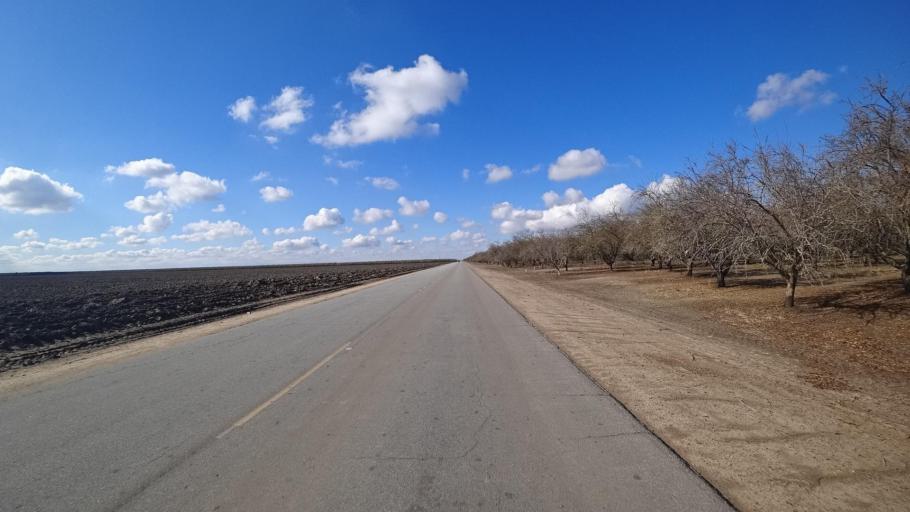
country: US
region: California
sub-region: Kern County
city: McFarland
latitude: 35.6742
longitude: -119.2877
